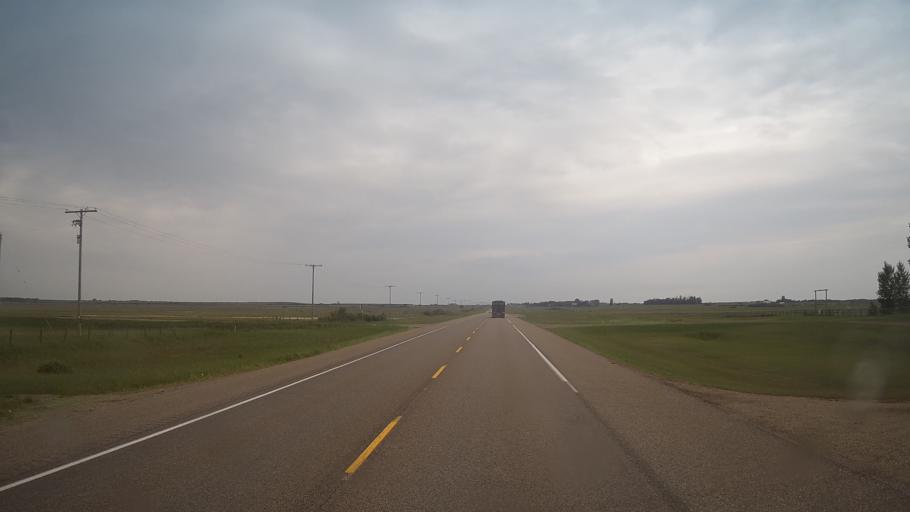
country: CA
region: Saskatchewan
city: Langham
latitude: 52.1289
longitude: -107.1446
